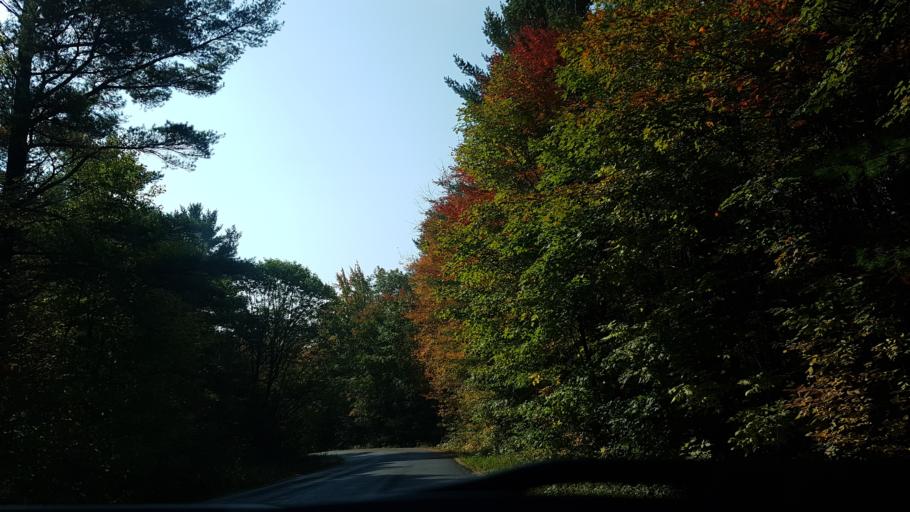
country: CA
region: Ontario
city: Bracebridge
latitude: 44.9753
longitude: -79.2597
